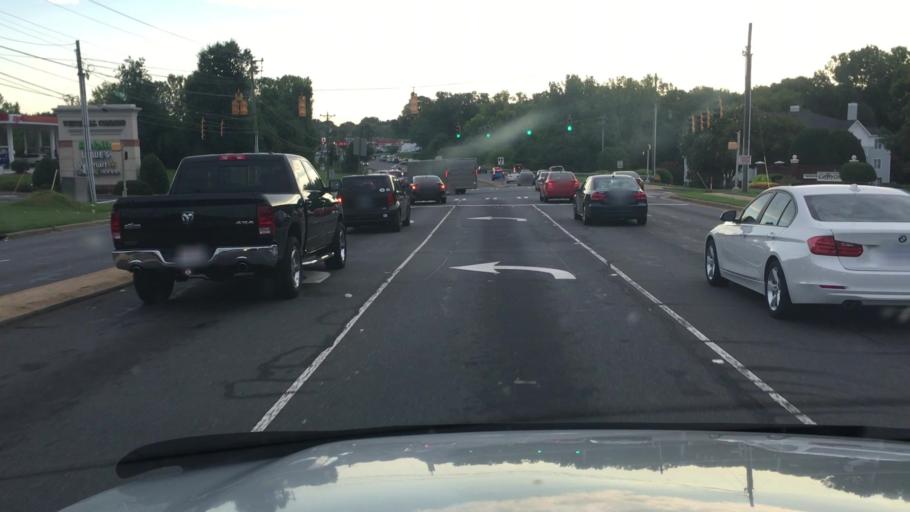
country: US
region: North Carolina
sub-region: Mecklenburg County
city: Pineville
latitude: 35.1437
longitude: -80.9290
